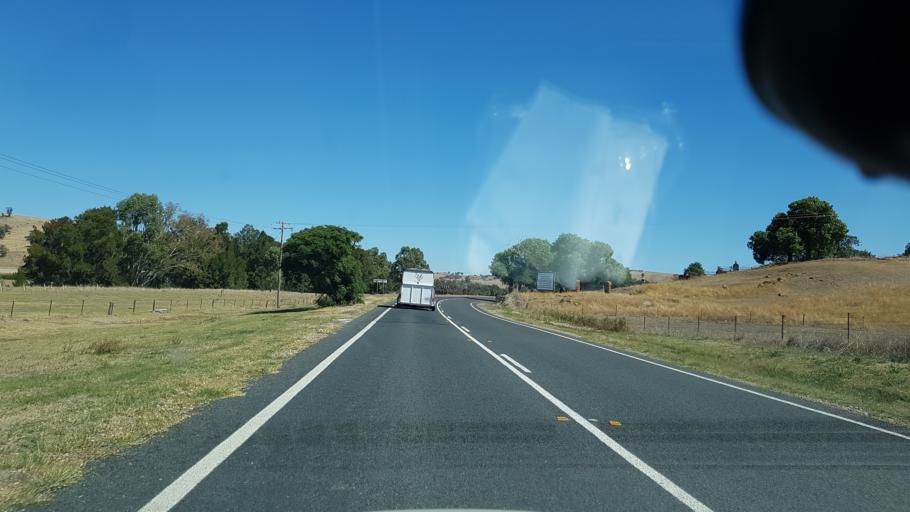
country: AU
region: New South Wales
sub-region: Gundagai
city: Gundagai
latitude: -34.8222
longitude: 148.3486
